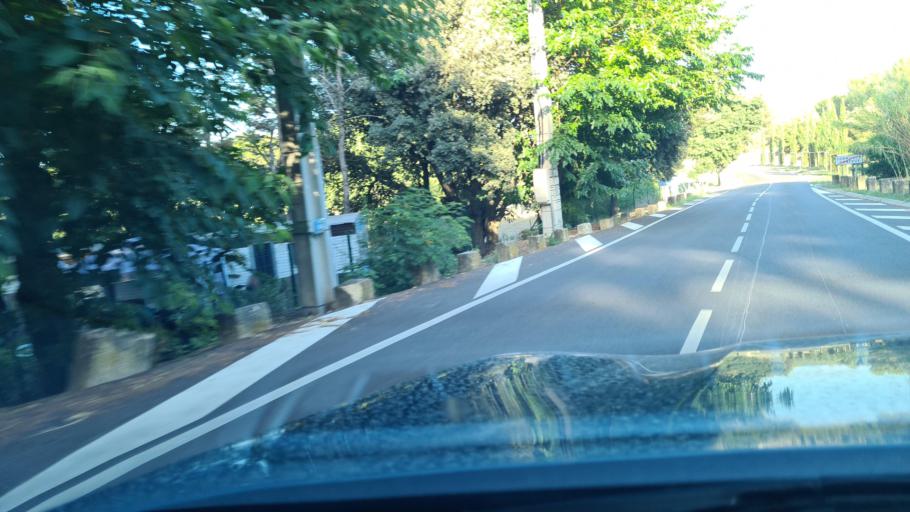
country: FR
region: Provence-Alpes-Cote d'Azur
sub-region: Departement des Bouches-du-Rhone
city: Cornillon-Confoux
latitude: 43.5695
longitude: 5.0720
